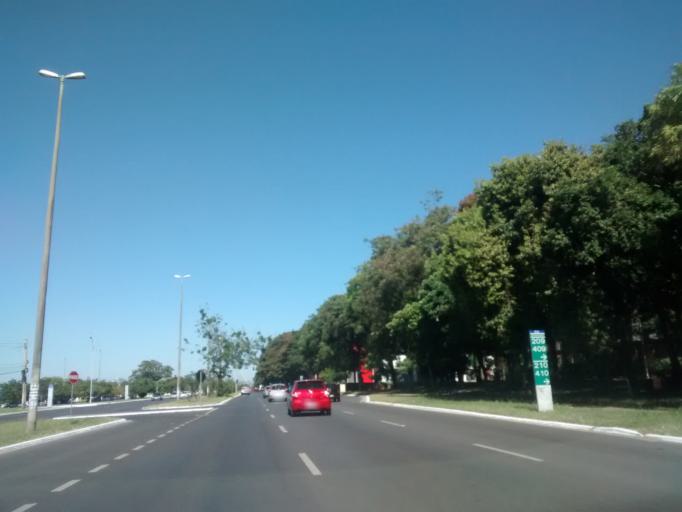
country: BR
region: Federal District
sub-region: Brasilia
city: Brasilia
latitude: -15.8235
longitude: -47.8989
